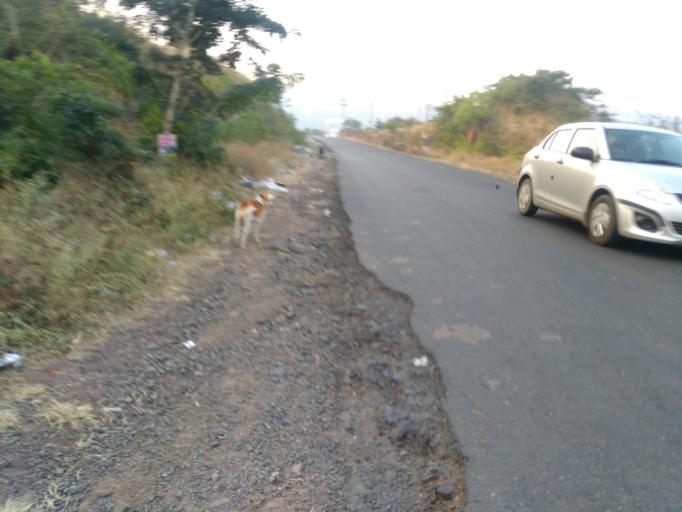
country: IN
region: Maharashtra
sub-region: Pune Division
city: Khed
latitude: 18.4239
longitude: 73.9019
